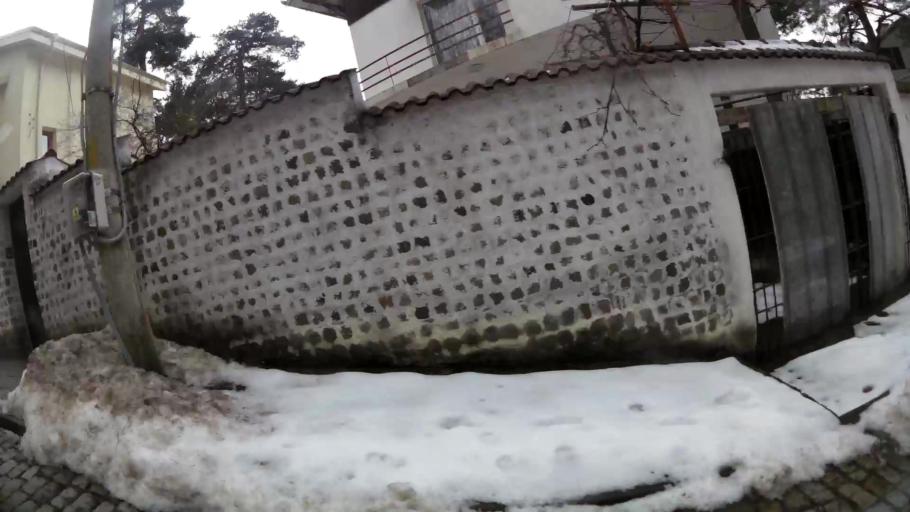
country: BG
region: Sofia-Capital
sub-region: Stolichna Obshtina
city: Sofia
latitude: 42.6556
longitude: 23.2380
